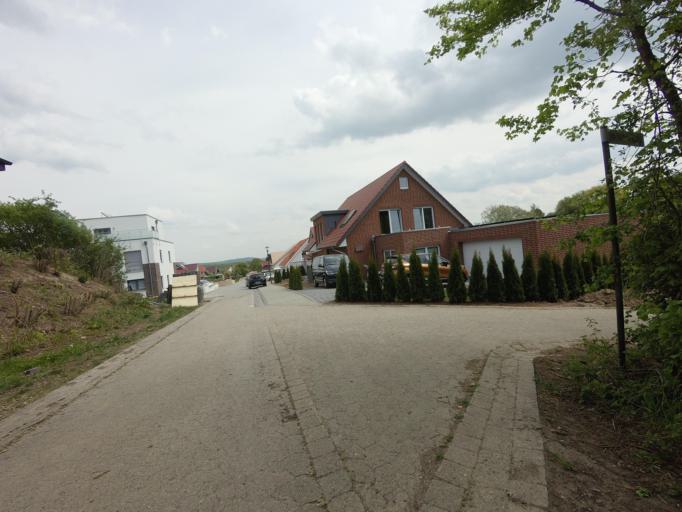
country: DE
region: Lower Saxony
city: Diekholzen
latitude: 52.1256
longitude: 9.9100
